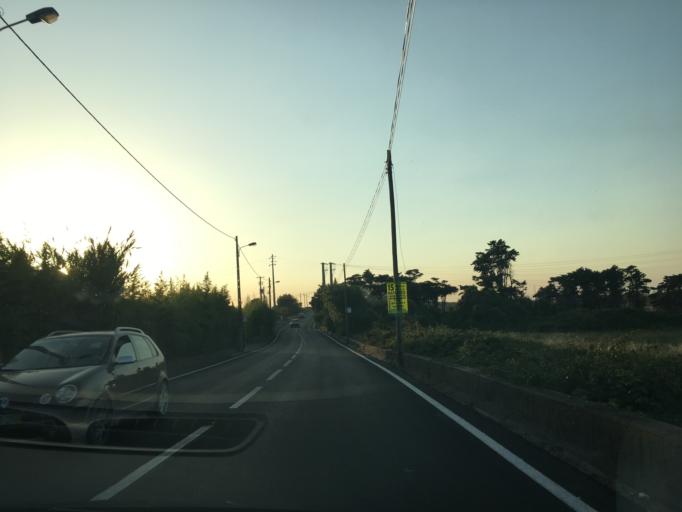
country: PT
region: Lisbon
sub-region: Sintra
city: Sintra
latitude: 38.8231
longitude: -9.4085
